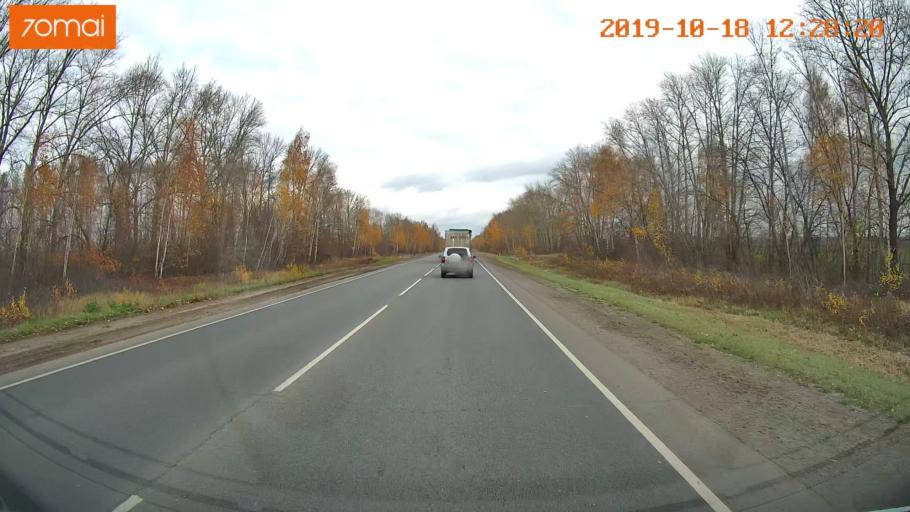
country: RU
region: Rjazan
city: Ryazan'
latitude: 54.5712
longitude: 39.5668
